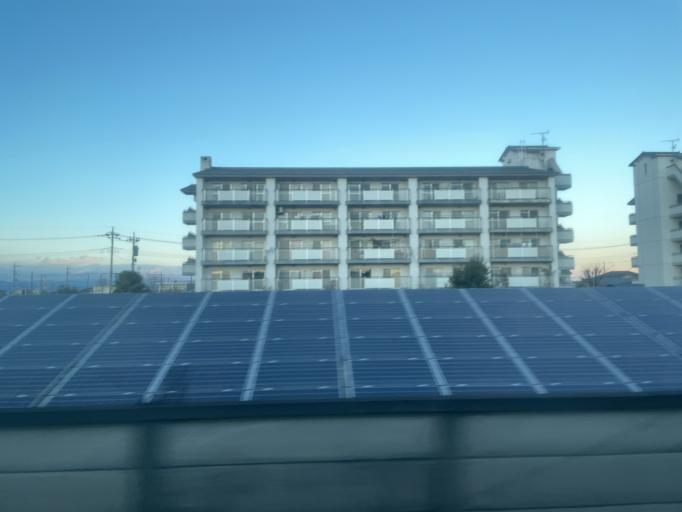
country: JP
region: Saitama
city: Fukayacho
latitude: 36.2036
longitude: 139.2427
